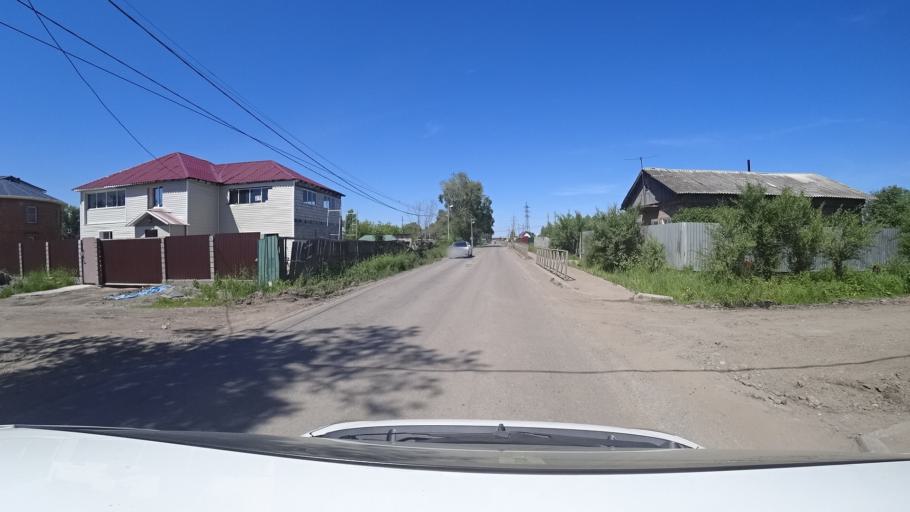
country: RU
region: Khabarovsk Krai
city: Topolevo
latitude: 48.4741
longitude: 135.1795
